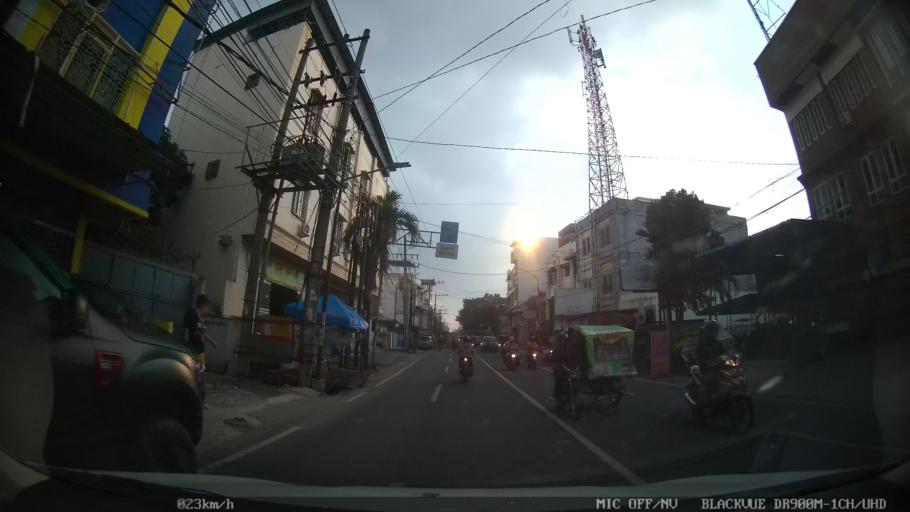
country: ID
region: North Sumatra
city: Medan
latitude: 3.5823
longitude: 98.6997
